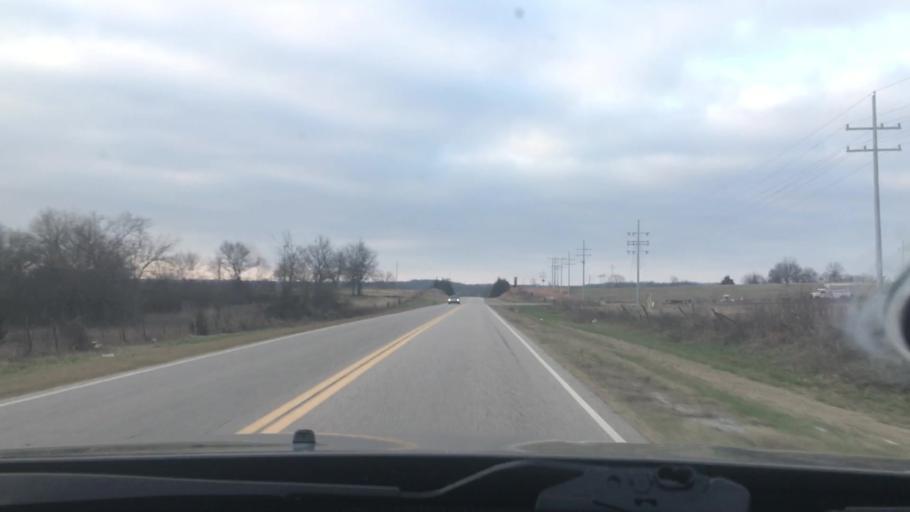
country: US
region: Oklahoma
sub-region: Pontotoc County
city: Ada
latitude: 34.6235
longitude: -96.6349
